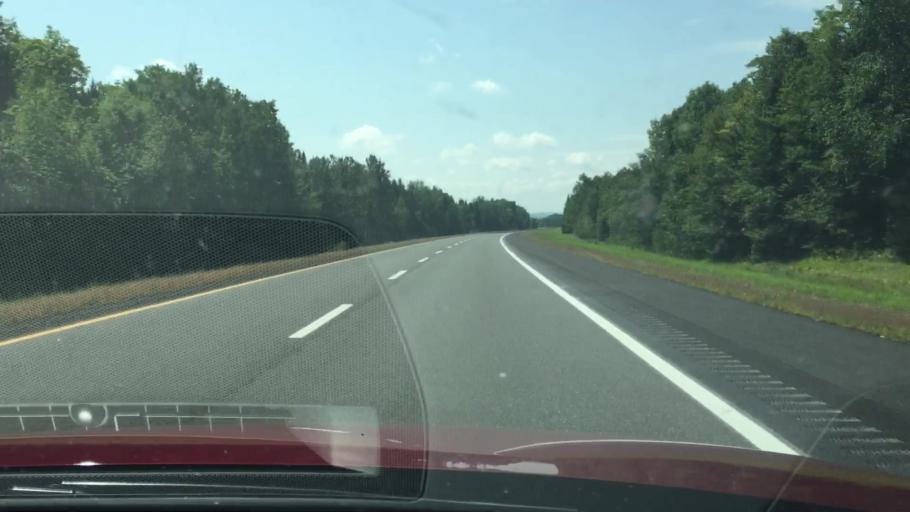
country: US
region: Maine
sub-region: Penobscot County
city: Patten
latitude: 45.9381
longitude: -68.3507
